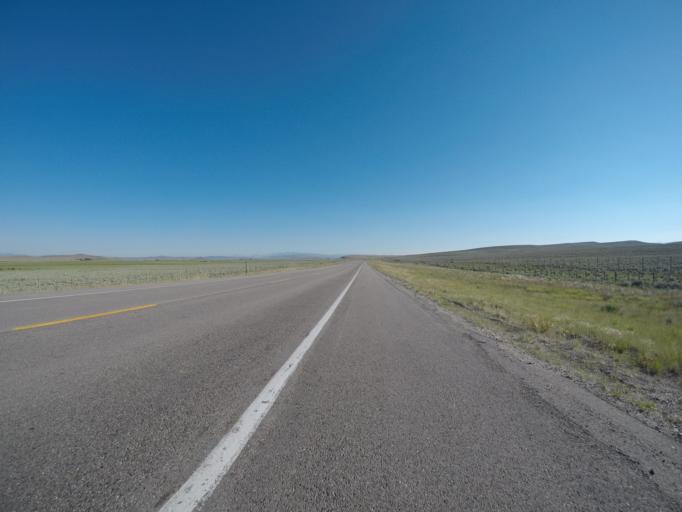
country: US
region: Wyoming
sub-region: Sublette County
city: Pinedale
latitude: 42.9262
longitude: -110.0808
